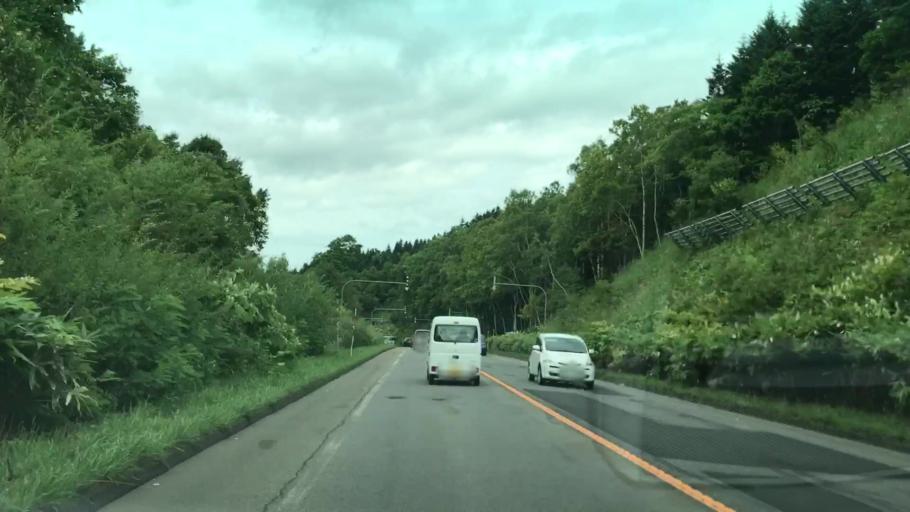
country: JP
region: Hokkaido
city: Niseko Town
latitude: 42.9310
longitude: 140.7129
